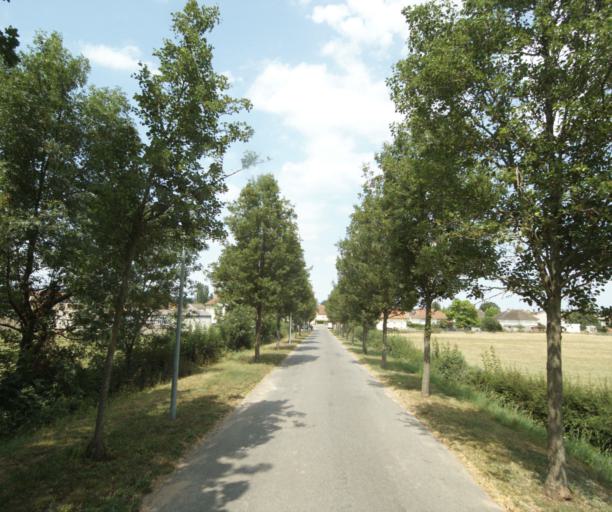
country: FR
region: Bourgogne
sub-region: Departement de Saone-et-Loire
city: Gueugnon
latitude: 46.5971
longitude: 4.0485
